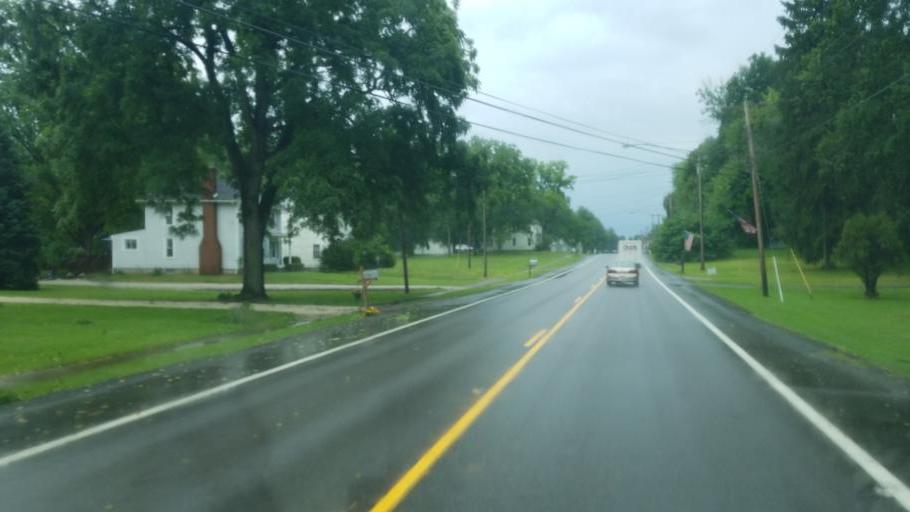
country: US
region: Ohio
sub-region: Trumbull County
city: Champion Heights
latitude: 41.3911
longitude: -80.8692
